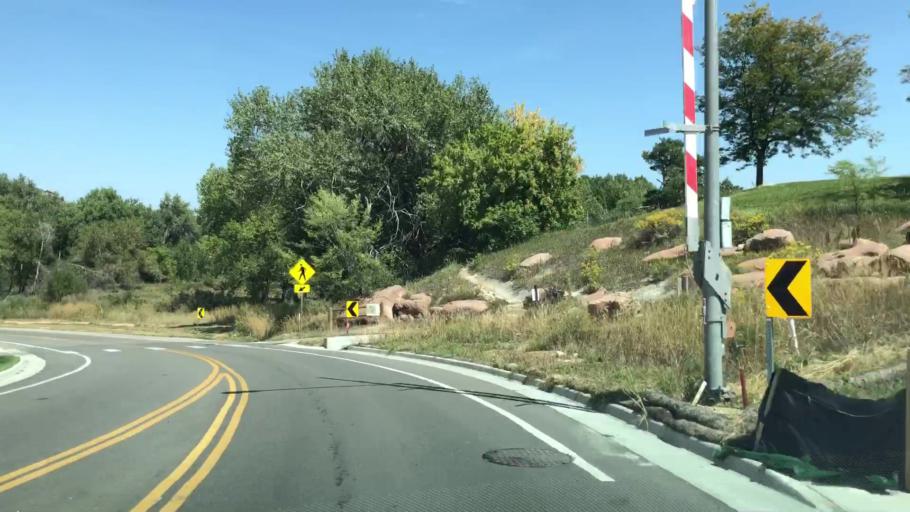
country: US
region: Colorado
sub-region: Larimer County
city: Loveland
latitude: 40.4023
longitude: -105.1410
